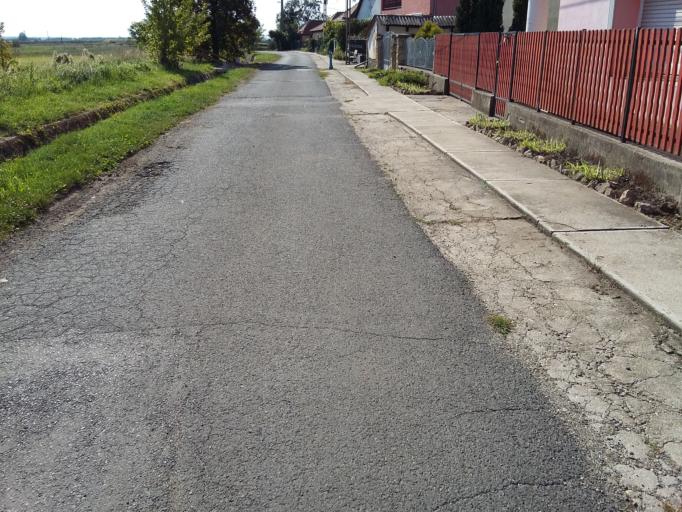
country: HU
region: Borsod-Abauj-Zemplen
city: Bekecs
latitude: 48.1499
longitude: 21.1737
